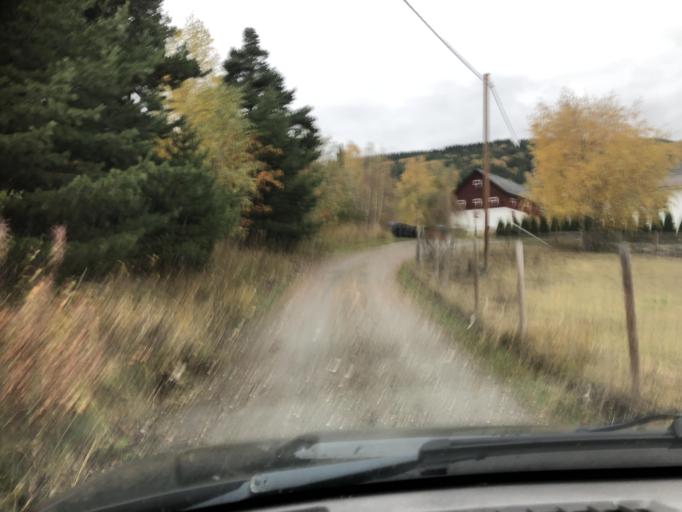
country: NO
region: Oppland
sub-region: Sor-Fron
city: Hundorp
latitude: 61.5743
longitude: 9.9140
